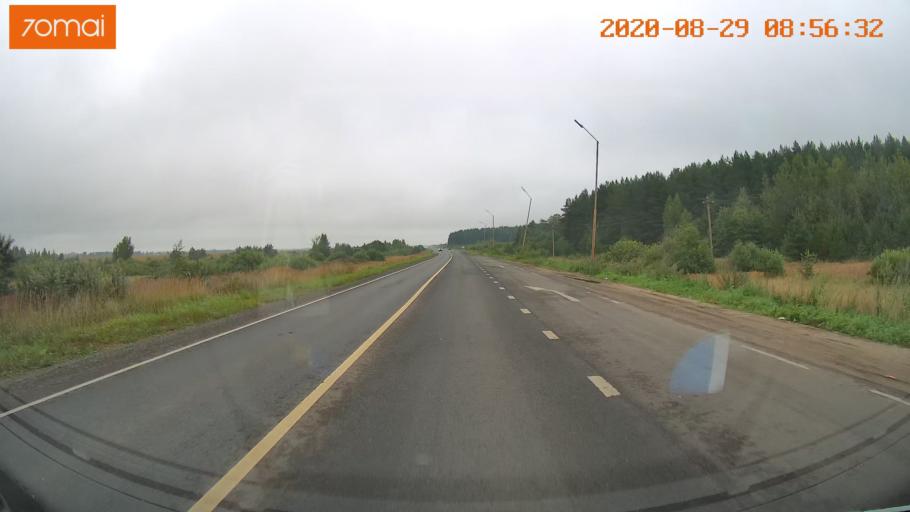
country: RU
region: Ivanovo
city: Staraya Vichuga
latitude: 57.2515
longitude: 41.8996
